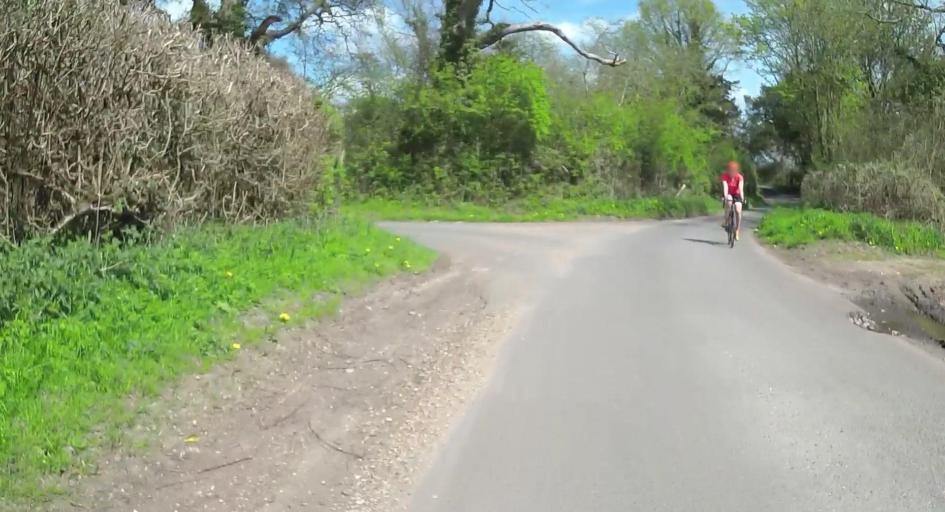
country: GB
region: England
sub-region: Hampshire
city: Romsey
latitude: 51.0489
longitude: -1.5373
